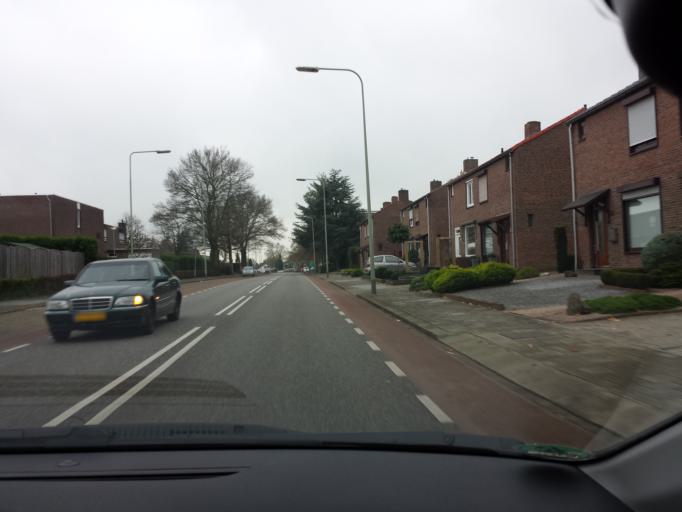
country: NL
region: Limburg
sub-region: Gemeente Kerkrade
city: Kerkrade
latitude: 50.9152
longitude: 6.0553
